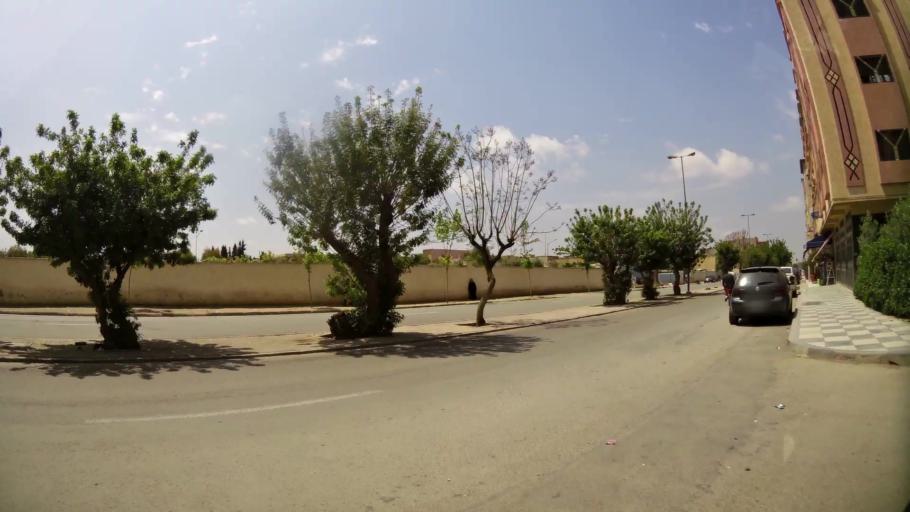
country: MA
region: Oriental
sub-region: Oujda-Angad
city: Oujda
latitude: 34.6840
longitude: -1.8801
